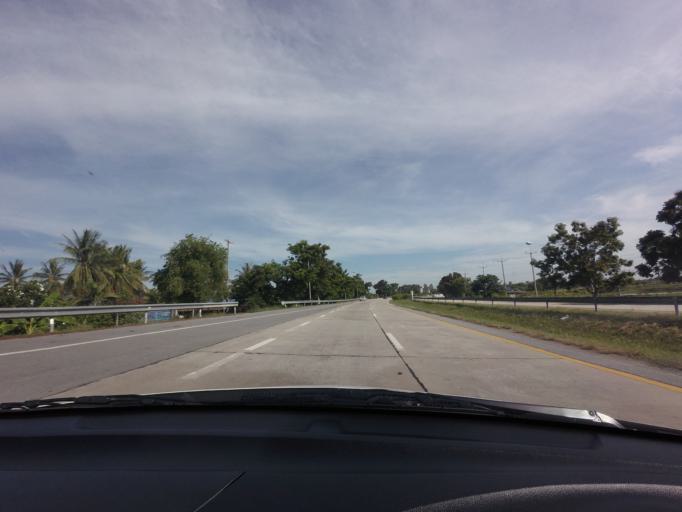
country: TH
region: Suphan Buri
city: Suphan Buri
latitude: 14.4691
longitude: 100.0407
